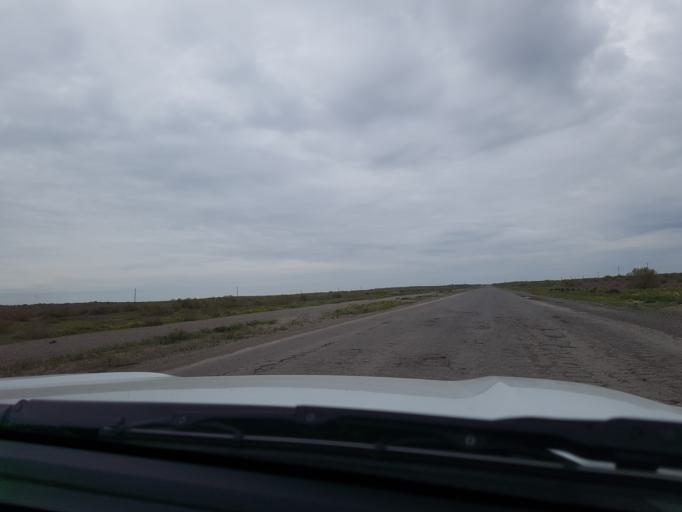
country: TM
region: Mary
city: Bayramaly
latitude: 37.9247
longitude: 62.6248
